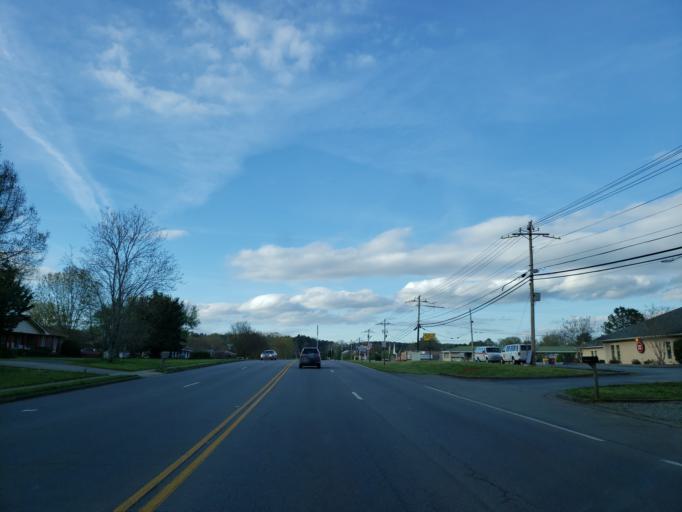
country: US
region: Georgia
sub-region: Bartow County
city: Cartersville
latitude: 34.2188
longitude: -84.8189
